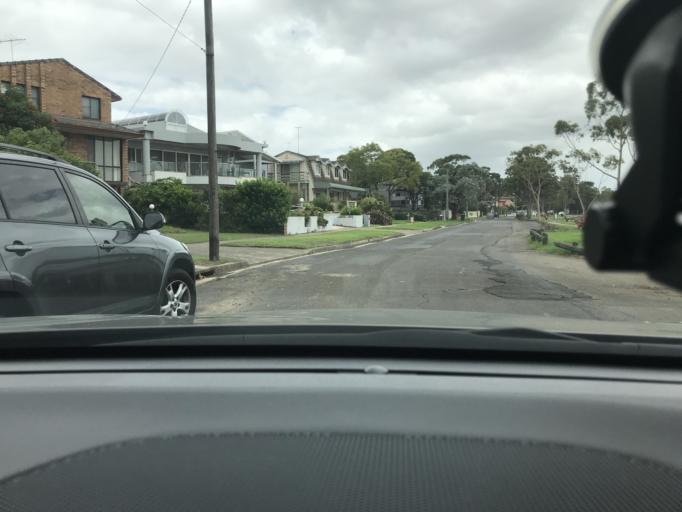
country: AU
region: New South Wales
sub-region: Canada Bay
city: Wareemba
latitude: -33.8547
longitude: 151.1267
